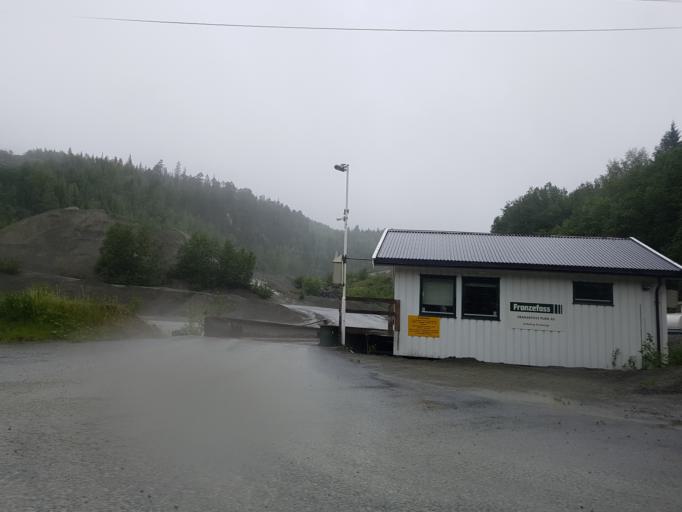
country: NO
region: Nord-Trondelag
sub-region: Stjordal
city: Stjordalshalsen
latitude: 63.3985
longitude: 10.9504
